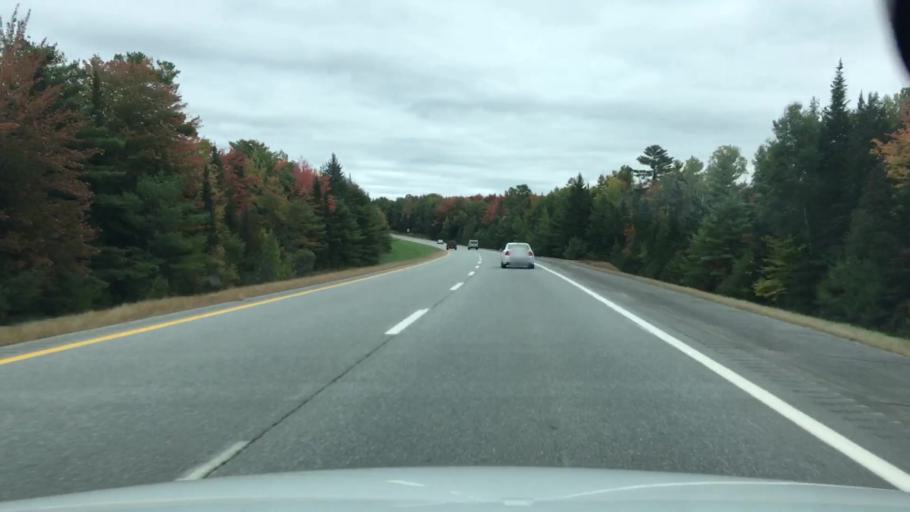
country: US
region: Maine
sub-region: Penobscot County
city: Plymouth
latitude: 44.7925
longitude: -69.2049
